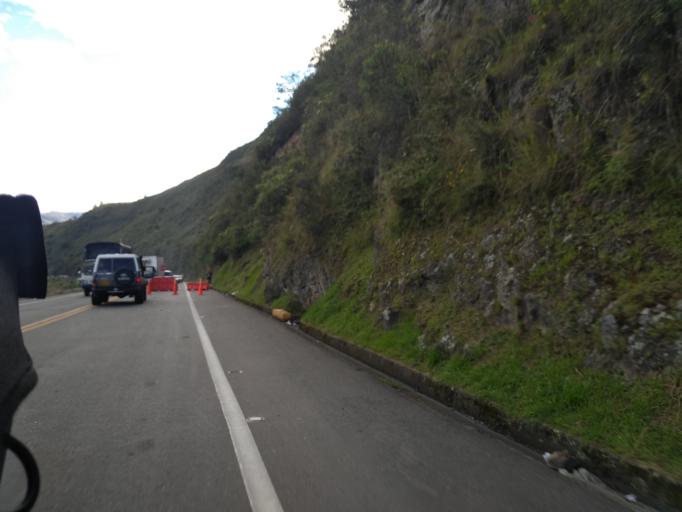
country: CO
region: Narino
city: Tangua
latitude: 1.0869
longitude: -77.4099
